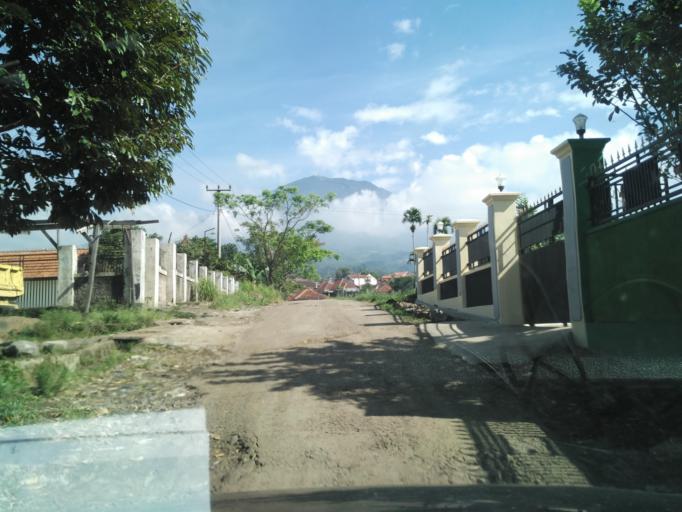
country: ID
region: West Java
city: Sukabumi
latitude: -6.8473
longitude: 107.0579
